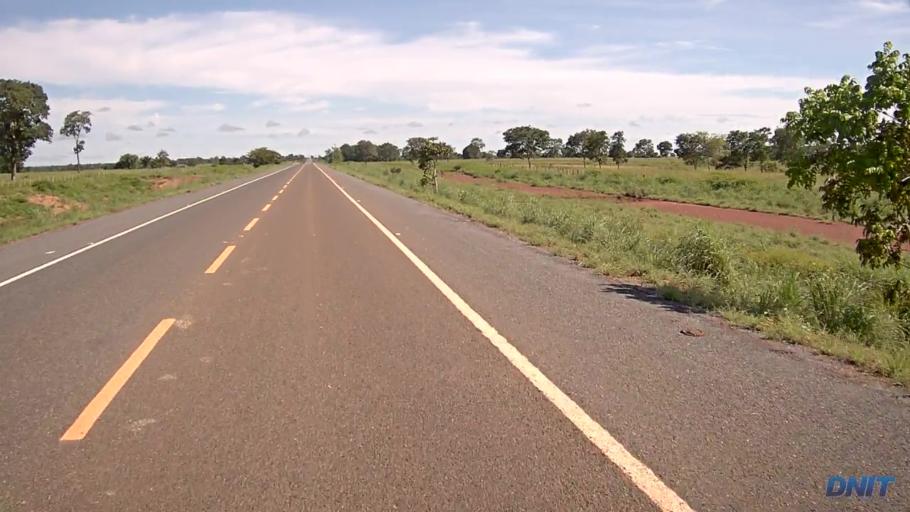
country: BR
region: Goias
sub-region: Sao Miguel Do Araguaia
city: Sao Miguel do Araguaia
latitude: -13.4656
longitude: -50.1163
